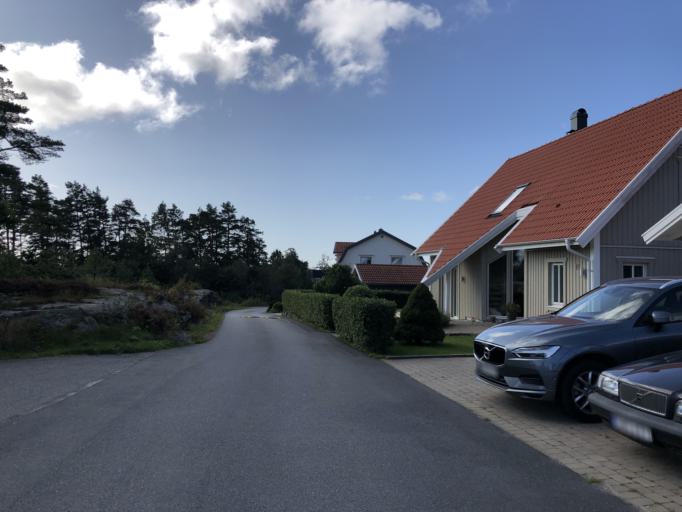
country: SE
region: Vaestra Goetaland
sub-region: Goteborg
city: Torslanda
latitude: 57.7483
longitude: 11.8218
